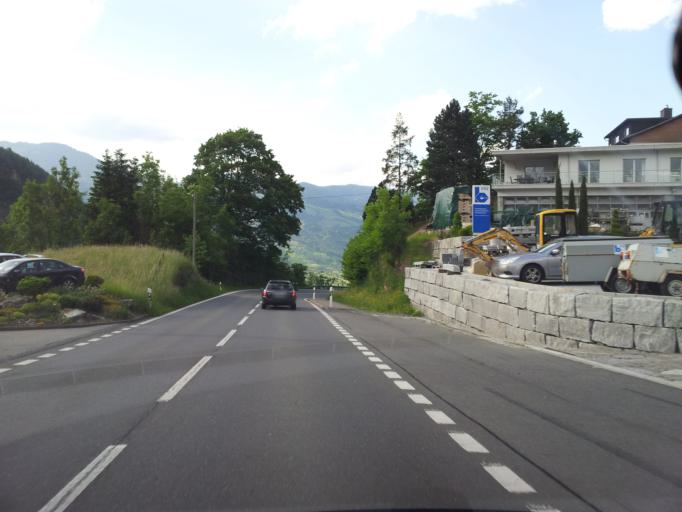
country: CH
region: Obwalden
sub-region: Obwalden
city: Giswil
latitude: 46.8158
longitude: 8.1750
